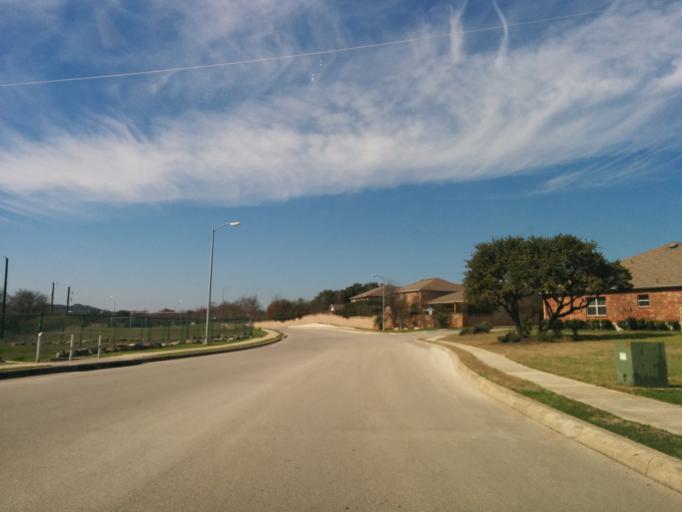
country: US
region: Texas
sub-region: Bexar County
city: Cross Mountain
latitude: 29.6676
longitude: -98.6359
